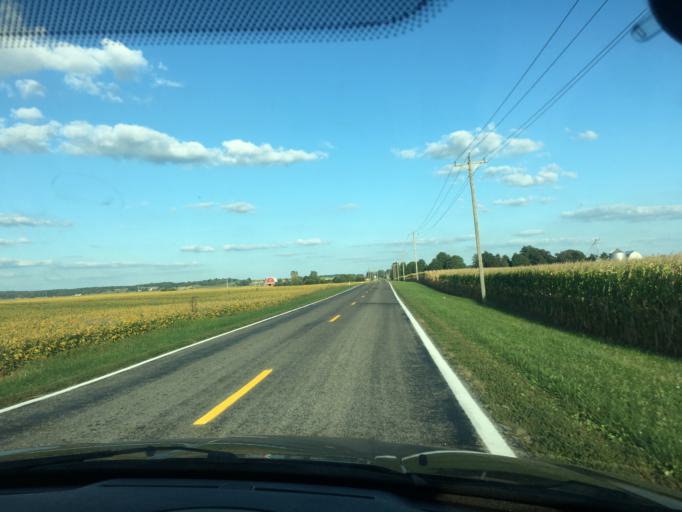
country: US
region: Ohio
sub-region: Logan County
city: West Liberty
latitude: 40.2219
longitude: -83.7613
